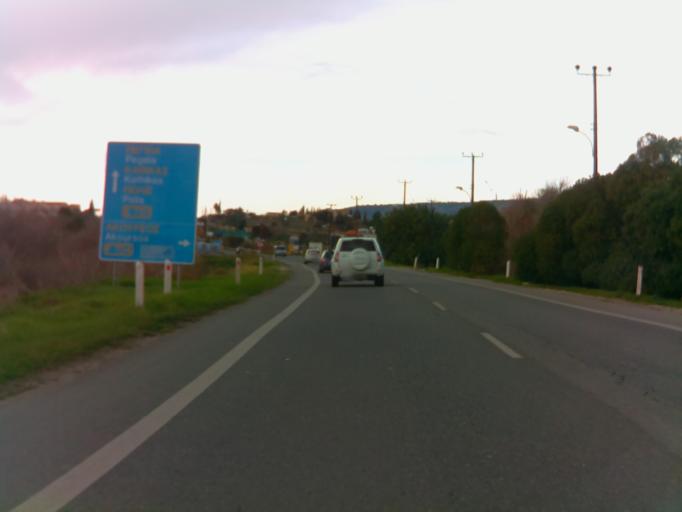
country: CY
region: Pafos
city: Kissonerga
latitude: 34.8488
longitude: 32.3851
